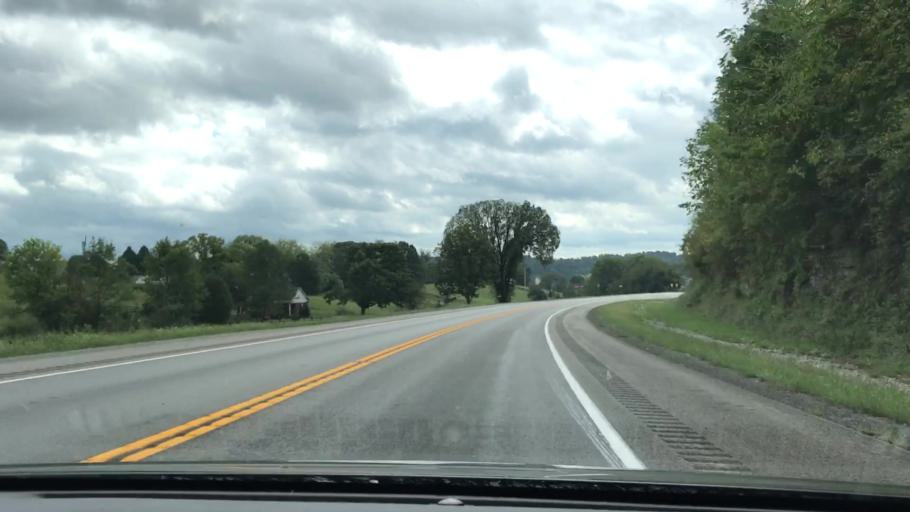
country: US
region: Kentucky
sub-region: Cumberland County
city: Burkesville
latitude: 36.7989
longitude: -85.3750
